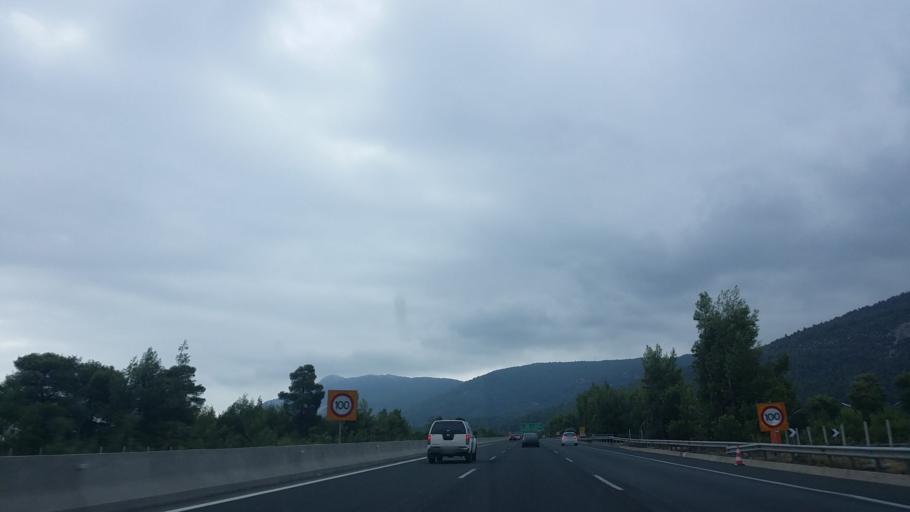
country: GR
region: Attica
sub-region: Nomarchia Anatolikis Attikis
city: Oropos
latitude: 38.2480
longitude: 23.7664
